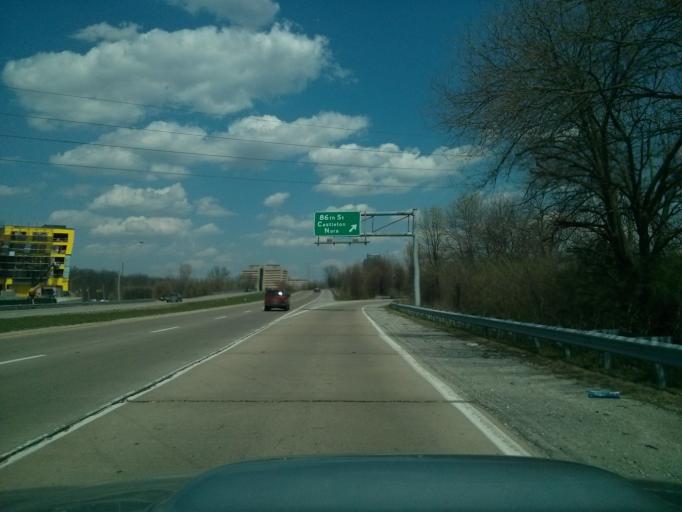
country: US
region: Indiana
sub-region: Marion County
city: Meridian Hills
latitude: 39.9092
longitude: -86.1166
